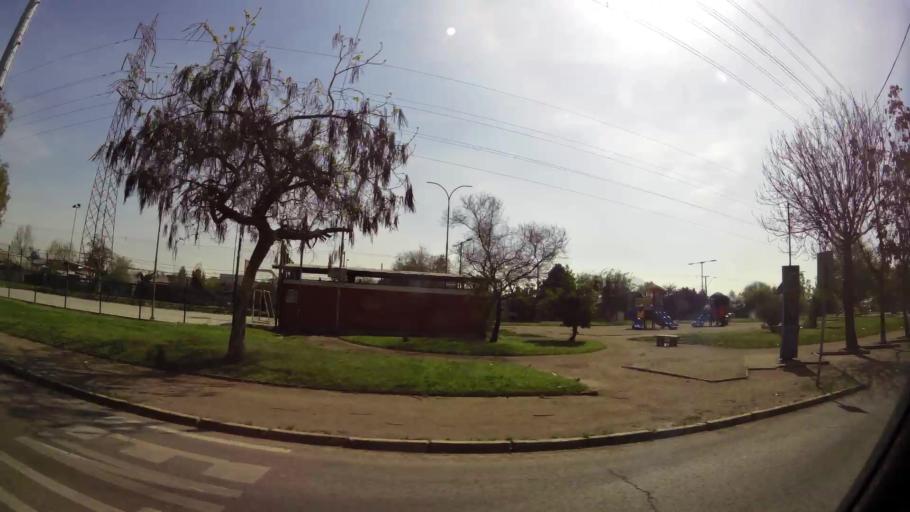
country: CL
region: Santiago Metropolitan
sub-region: Provincia de Santiago
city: Lo Prado
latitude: -33.4225
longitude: -70.7424
